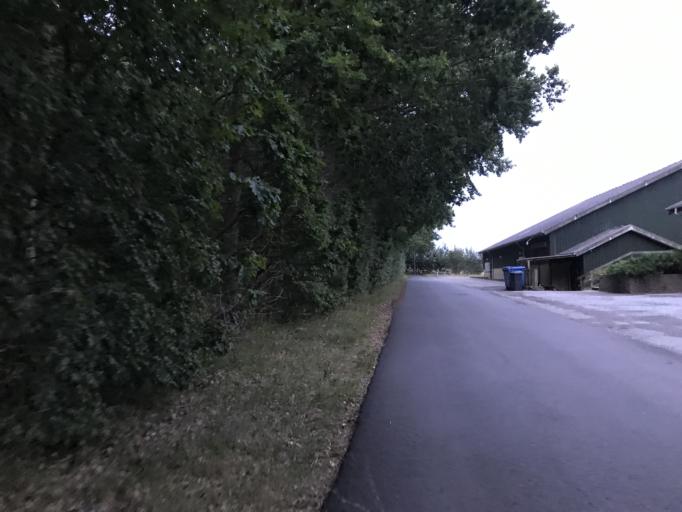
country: DK
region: South Denmark
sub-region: Faaborg-Midtfyn Kommune
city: Faaborg
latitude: 54.9353
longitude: 10.2470
